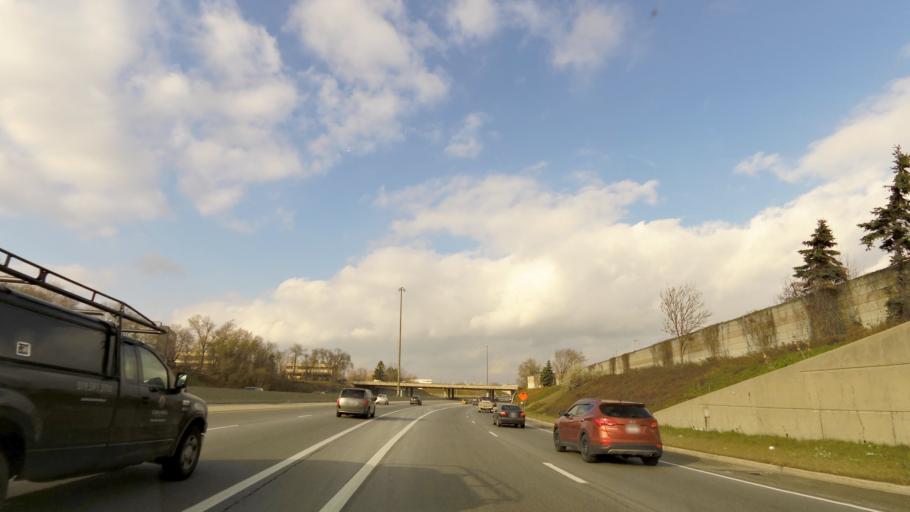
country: CA
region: Ontario
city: Waterloo
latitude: 43.4569
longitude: -80.4707
